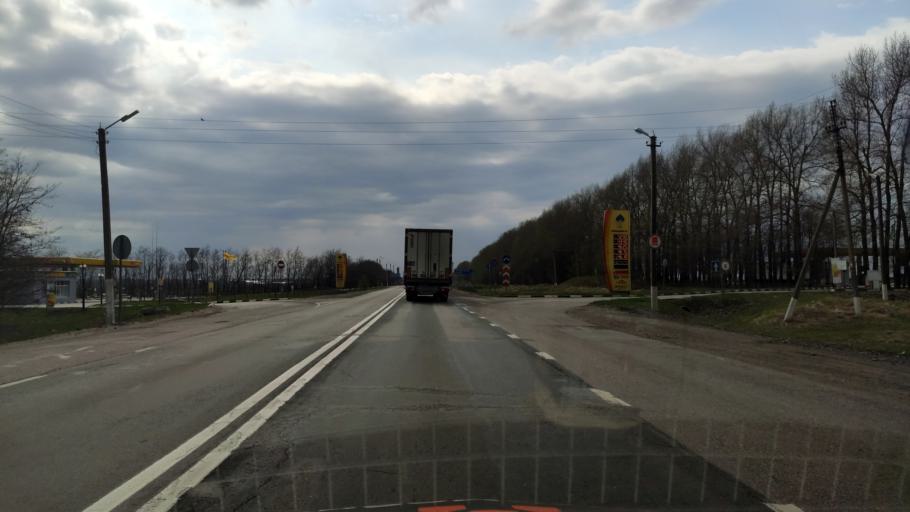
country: RU
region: Voronezj
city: Nizhnedevitsk
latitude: 51.5623
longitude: 38.2550
